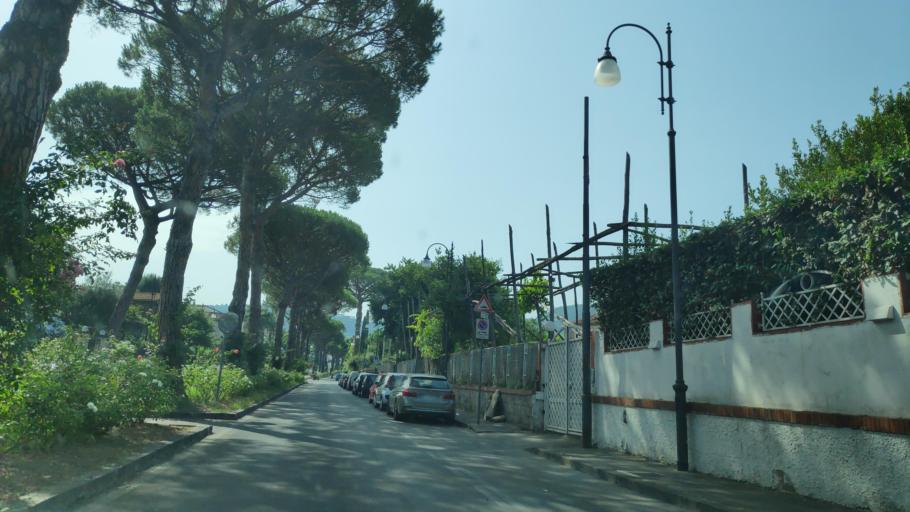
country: IT
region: Campania
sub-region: Provincia di Napoli
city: Sant'Agnello
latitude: 40.6348
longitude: 14.3954
